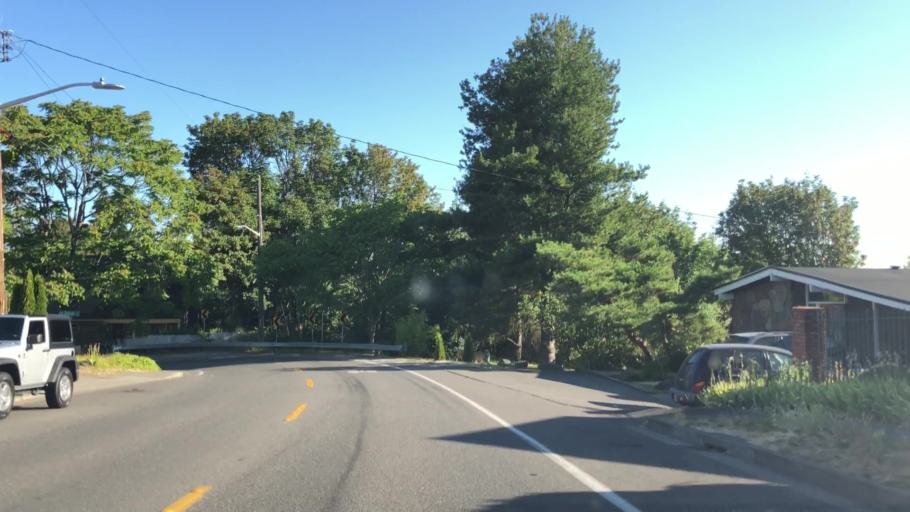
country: US
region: Washington
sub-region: King County
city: White Center
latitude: 47.5557
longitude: -122.3548
